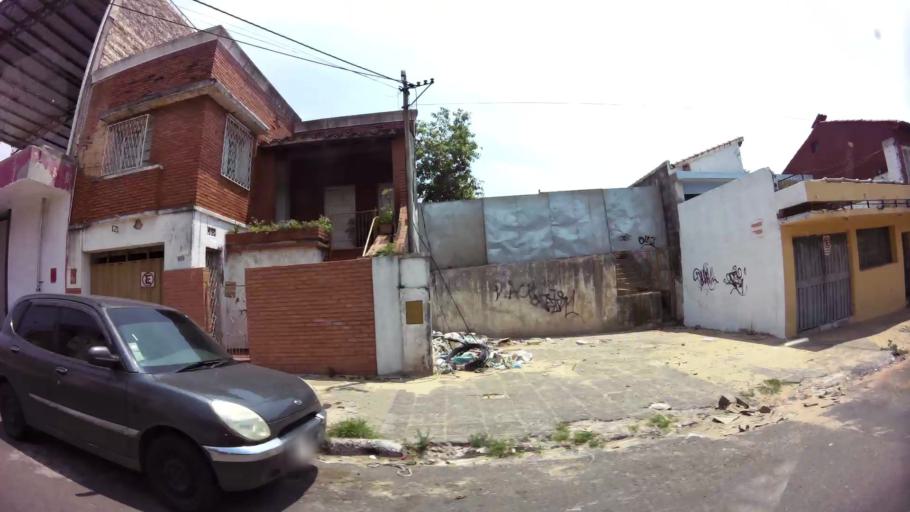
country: PY
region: Asuncion
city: Asuncion
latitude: -25.2969
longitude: -57.6194
